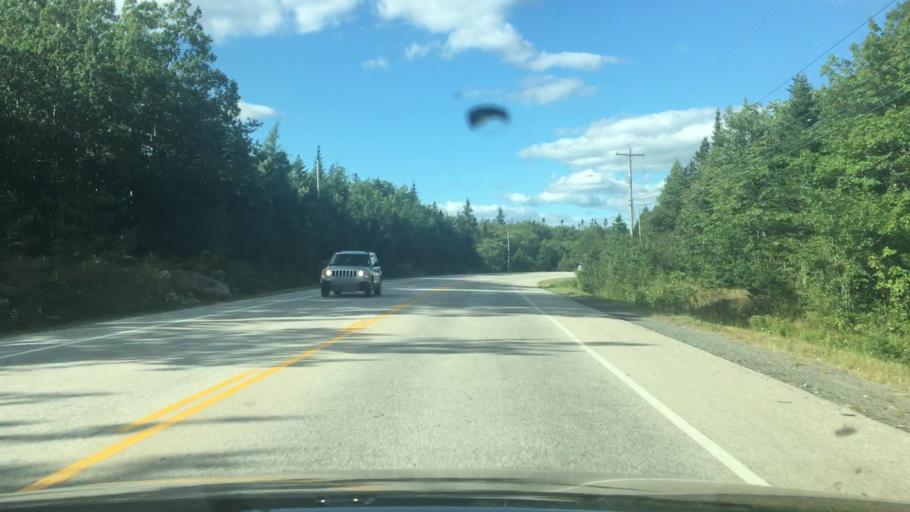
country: CA
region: Nova Scotia
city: Halifax
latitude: 44.6141
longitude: -63.6698
